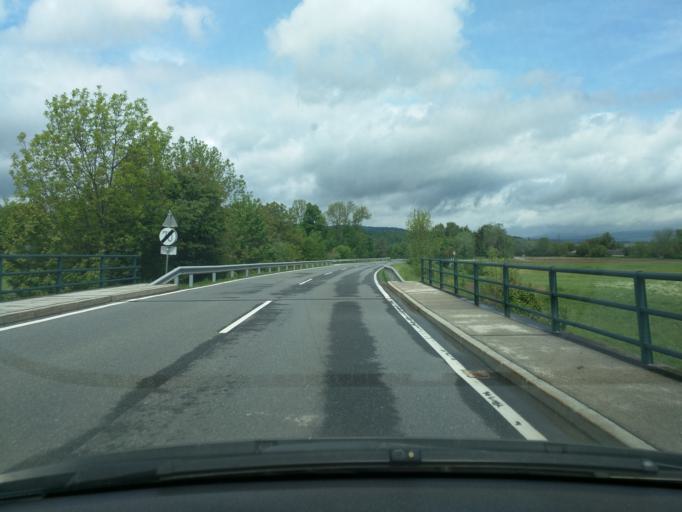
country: AT
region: Lower Austria
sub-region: Politischer Bezirk Melk
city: Blindenmarkt
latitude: 48.1164
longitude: 15.0124
